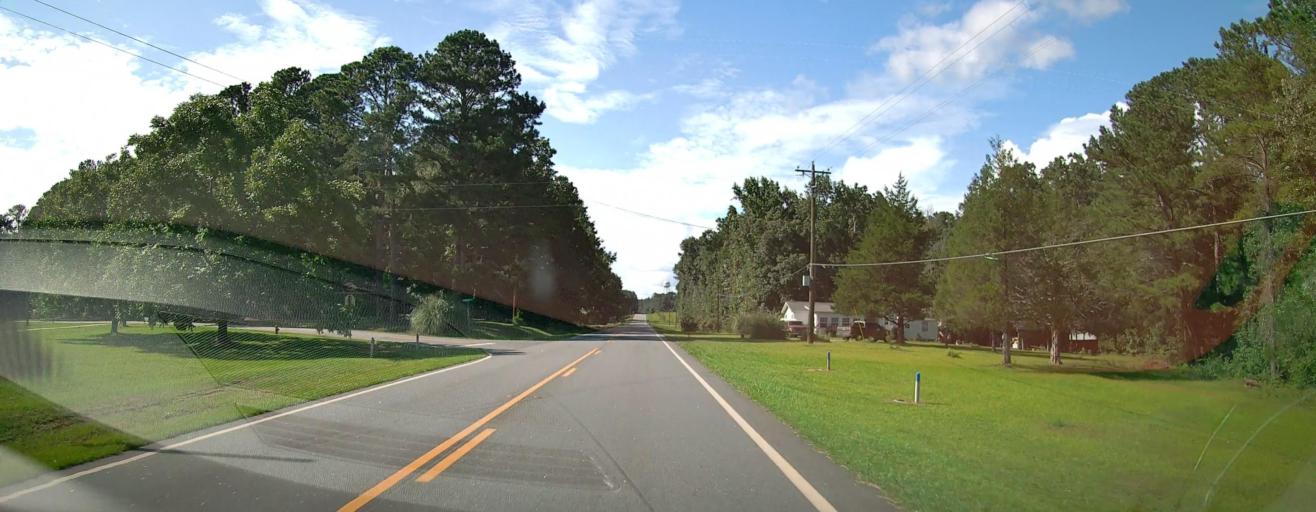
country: US
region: Georgia
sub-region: Upson County
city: Hannahs Mill
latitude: 32.9046
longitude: -84.4233
